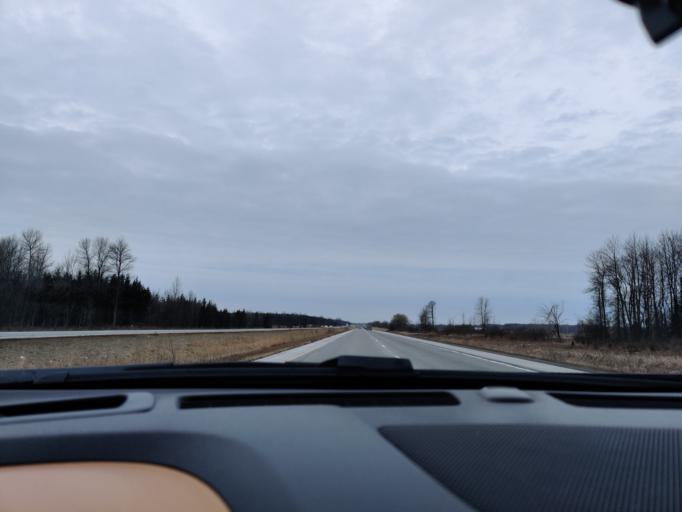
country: US
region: New York
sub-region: St. Lawrence County
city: Ogdensburg
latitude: 44.8835
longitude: -75.2796
